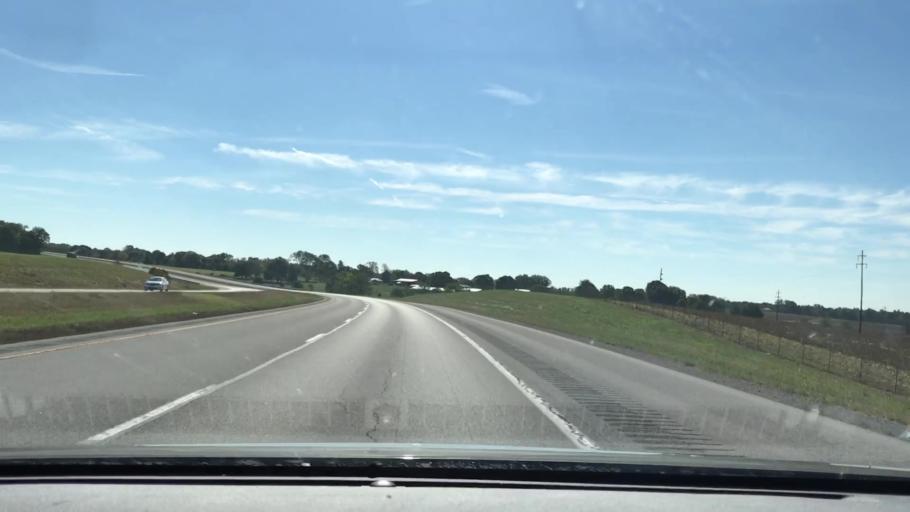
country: US
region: Kentucky
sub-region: Todd County
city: Elkton
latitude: 36.8133
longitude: -87.1393
